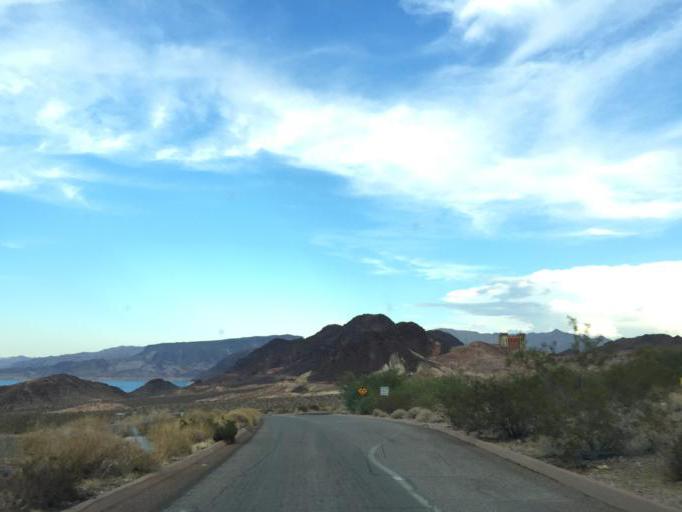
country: US
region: Nevada
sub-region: Clark County
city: Boulder City
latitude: 36.0105
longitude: -114.7973
